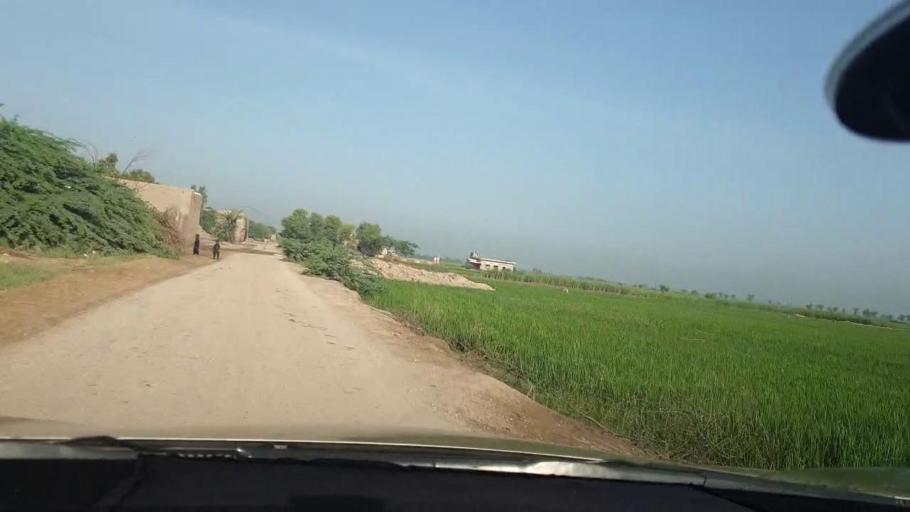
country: PK
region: Sindh
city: Kambar
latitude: 27.6545
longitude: 68.0324
